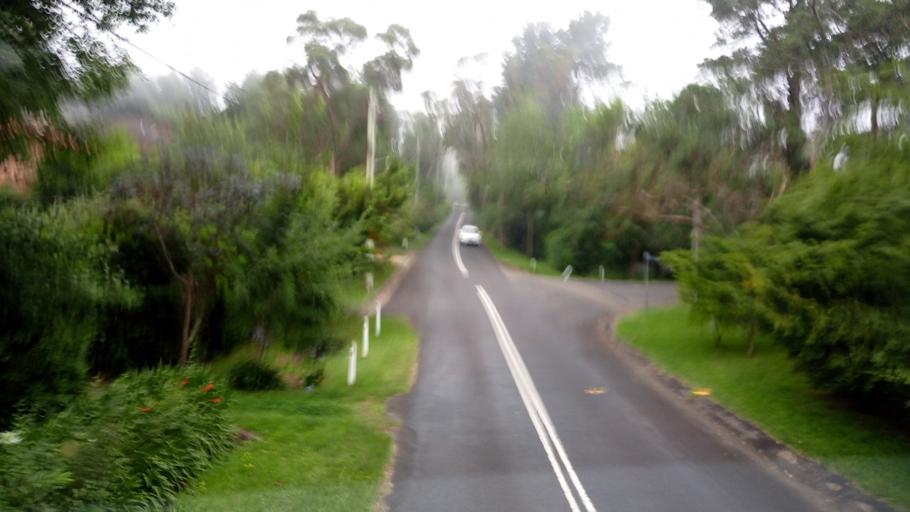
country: AU
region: New South Wales
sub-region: Blue Mountains Municipality
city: Leura
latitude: -33.7188
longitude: 150.3391
